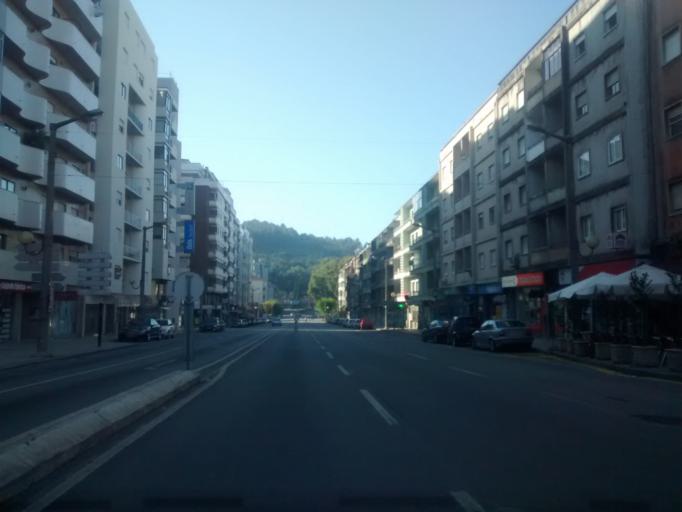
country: PT
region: Braga
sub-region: Braga
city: Braga
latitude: 41.5458
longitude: -8.4197
